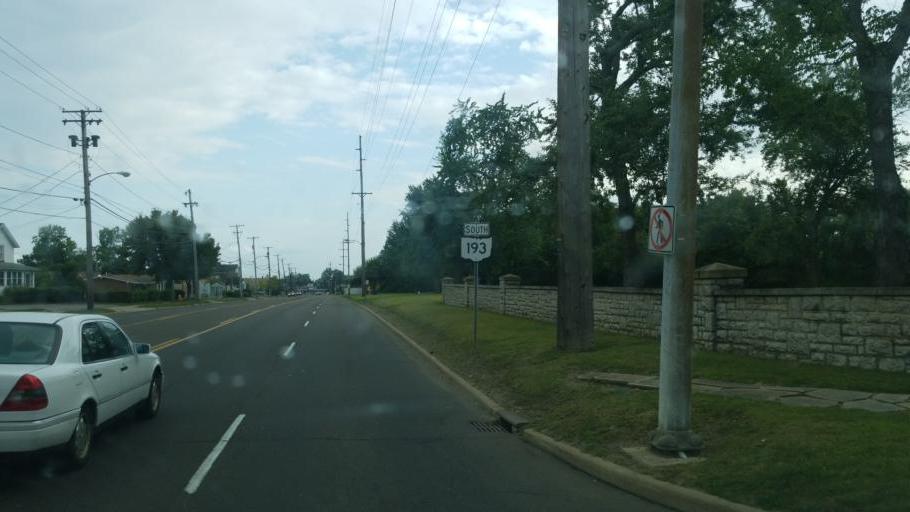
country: US
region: Ohio
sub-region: Mahoning County
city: Youngstown
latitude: 41.1286
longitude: -80.6649
